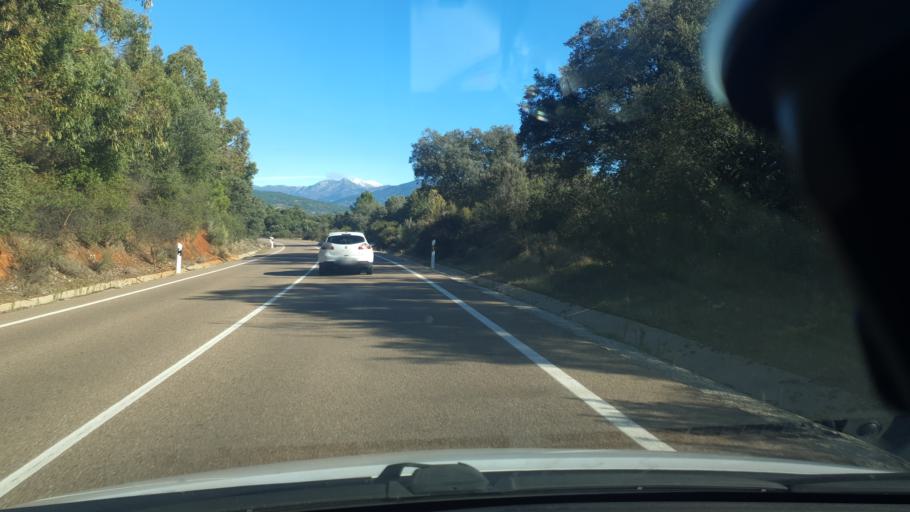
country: ES
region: Castille and Leon
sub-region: Provincia de Avila
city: Arenas de San Pedro
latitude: 40.1654
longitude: -5.1052
